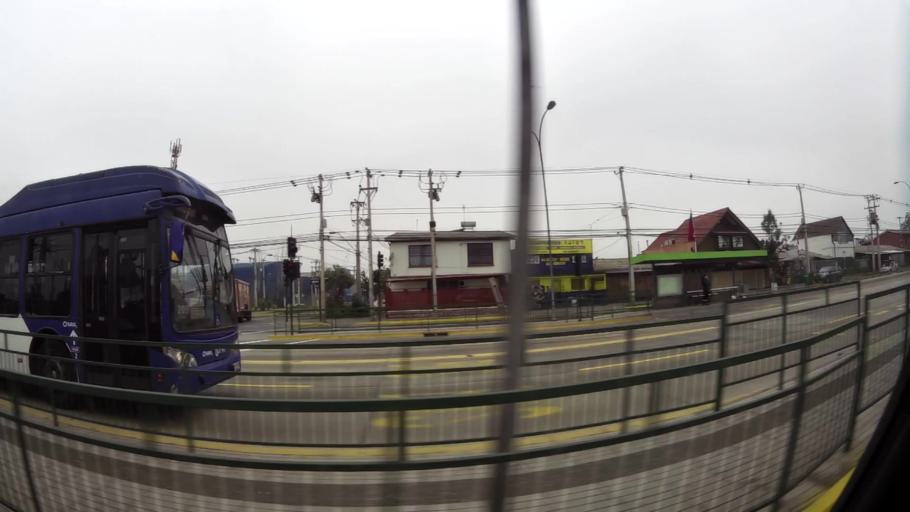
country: CL
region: Santiago Metropolitan
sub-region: Provincia de Santiago
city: Santiago
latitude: -33.4956
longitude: -70.6399
